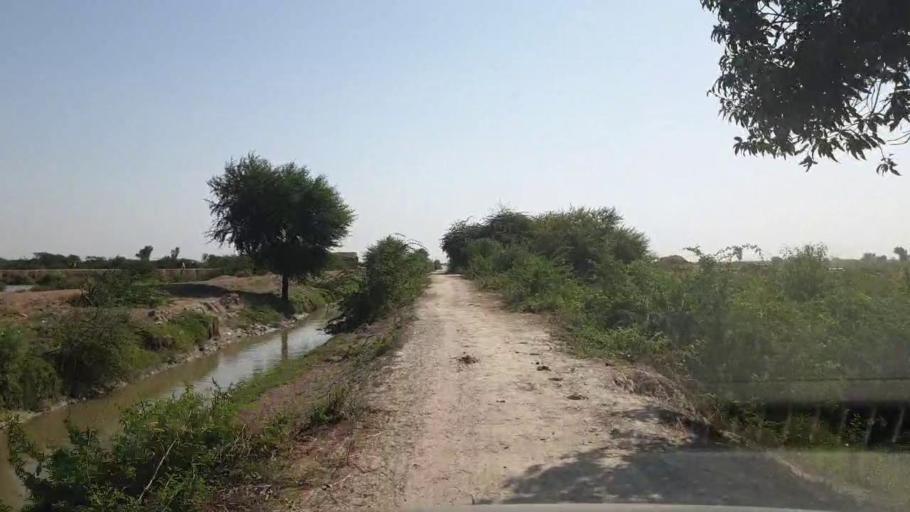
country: PK
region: Sindh
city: Kadhan
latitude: 24.6170
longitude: 68.9972
